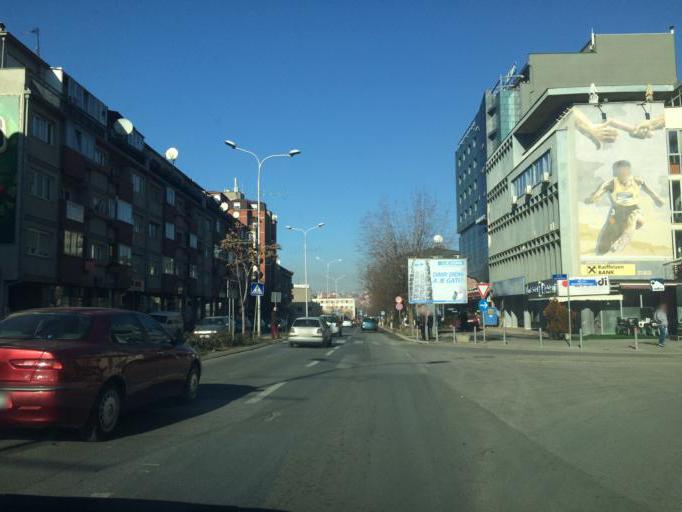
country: XK
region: Pristina
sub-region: Komuna e Prishtines
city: Pristina
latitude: 42.6610
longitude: 21.1650
